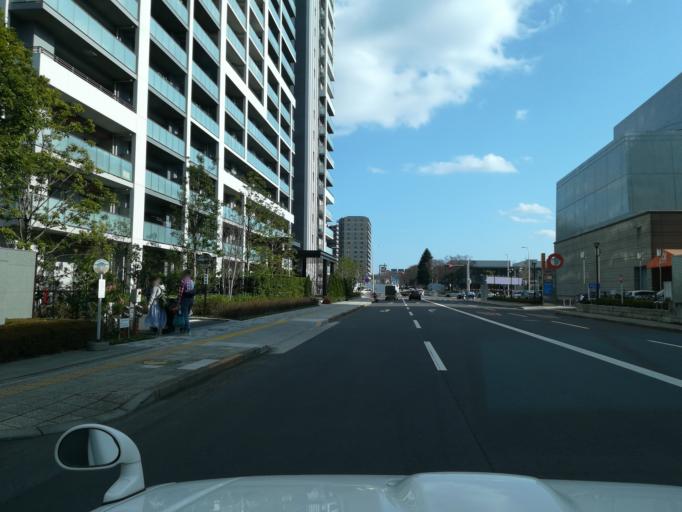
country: JP
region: Ibaraki
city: Naka
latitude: 36.0822
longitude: 140.1144
